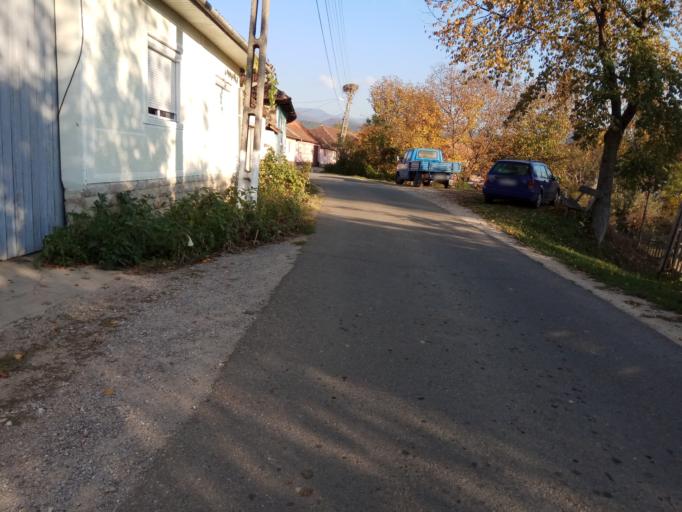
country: RO
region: Bihor
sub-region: Comuna Budureasa
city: Budureasa
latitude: 46.6962
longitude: 22.4737
